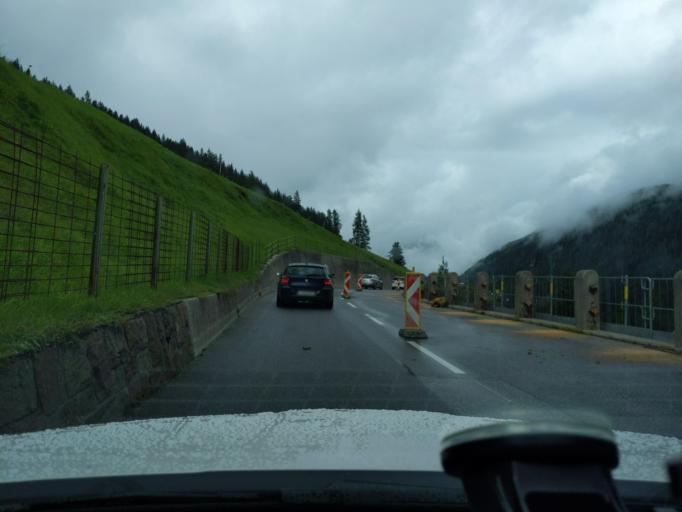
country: AT
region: Tyrol
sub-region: Politischer Bezirk Innsbruck Land
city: Schmirn
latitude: 47.1164
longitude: 11.6849
